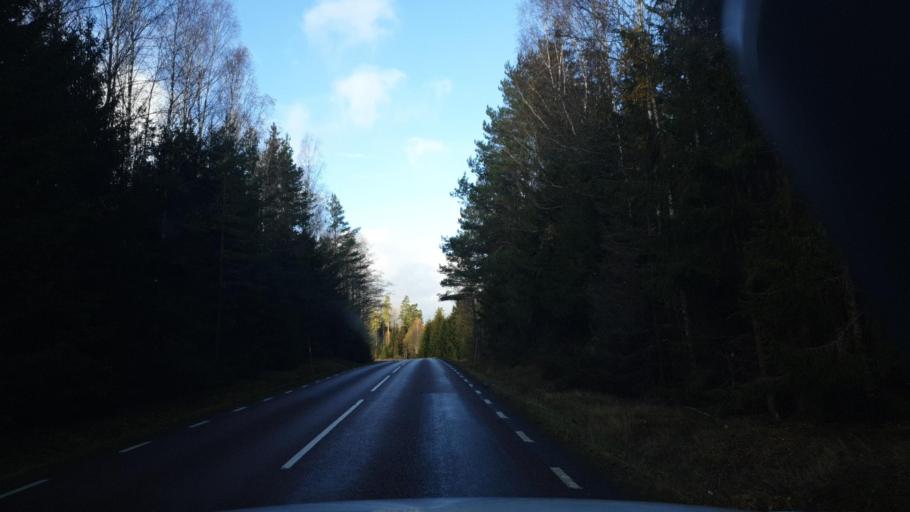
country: SE
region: Vaermland
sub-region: Grums Kommun
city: Grums
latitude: 59.4597
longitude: 12.9527
